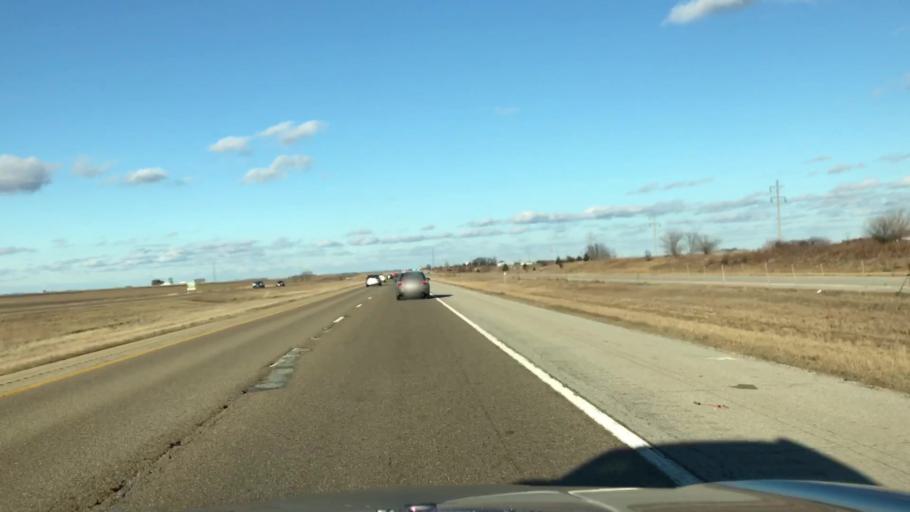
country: US
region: Illinois
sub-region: McLean County
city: Chenoa
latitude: 40.7061
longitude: -88.7457
